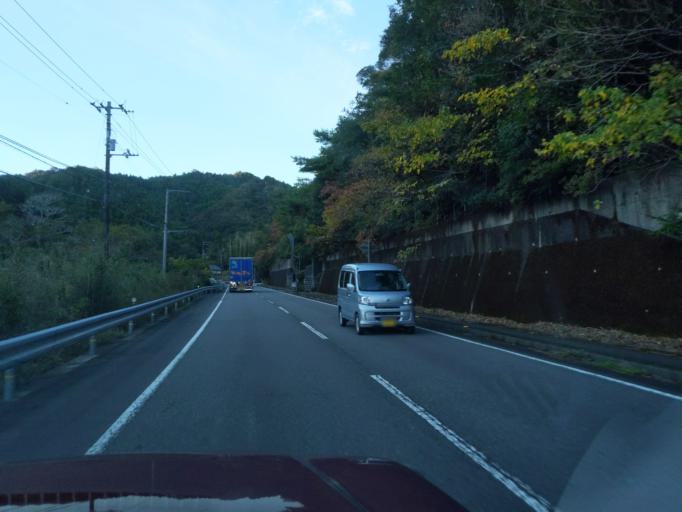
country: JP
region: Tokushima
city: Anan
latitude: 33.7145
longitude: 134.4816
